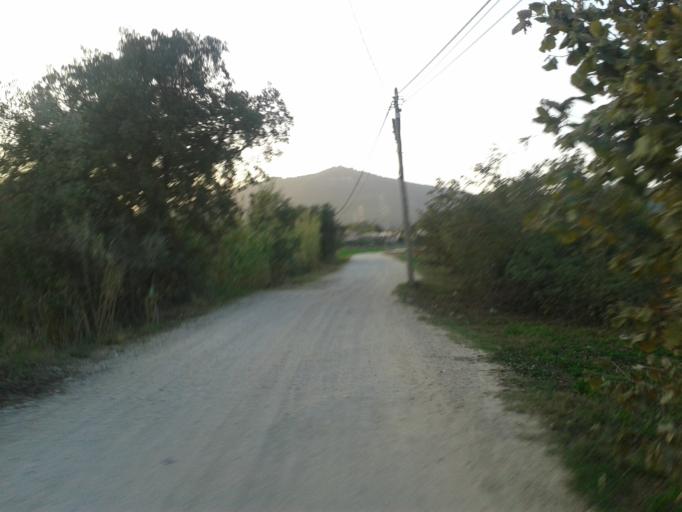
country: ES
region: Catalonia
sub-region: Provincia de Barcelona
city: Sentmenat
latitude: 41.6137
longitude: 2.1290
